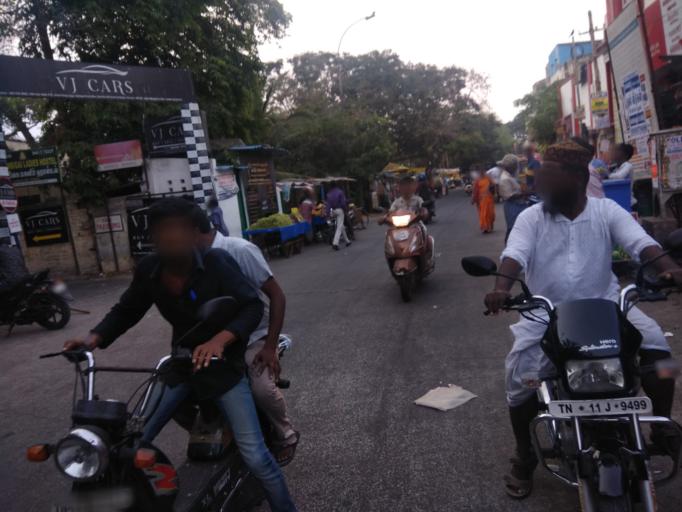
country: IN
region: Tamil Nadu
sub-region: Kancheepuram
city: Alandur
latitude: 13.0222
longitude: 80.2242
